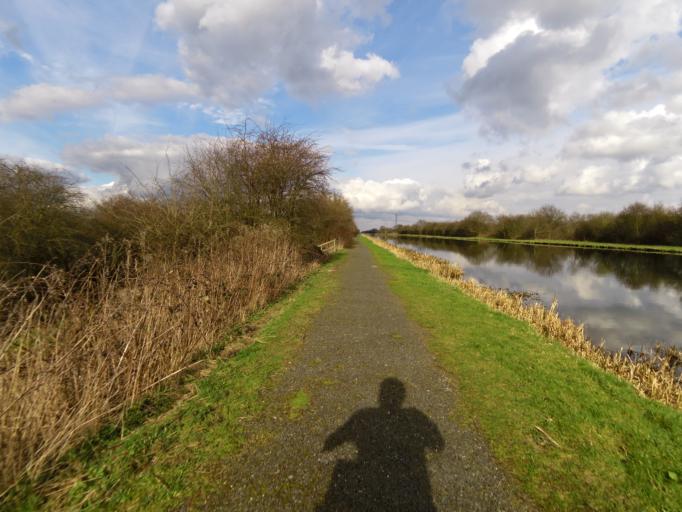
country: GB
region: England
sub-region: Doncaster
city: Stainforth
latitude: 53.6263
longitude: -1.0457
